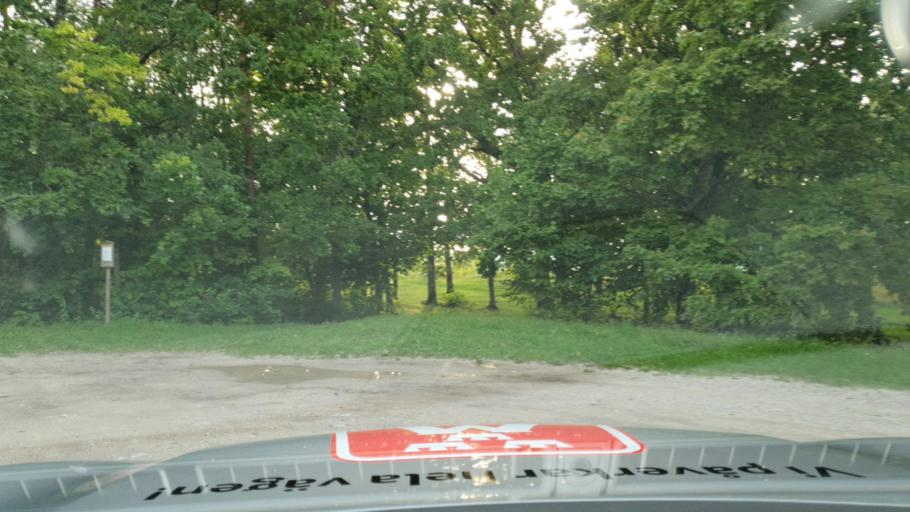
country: SE
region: Gotland
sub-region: Gotland
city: Klintehamn
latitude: 57.3800
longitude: 18.2362
